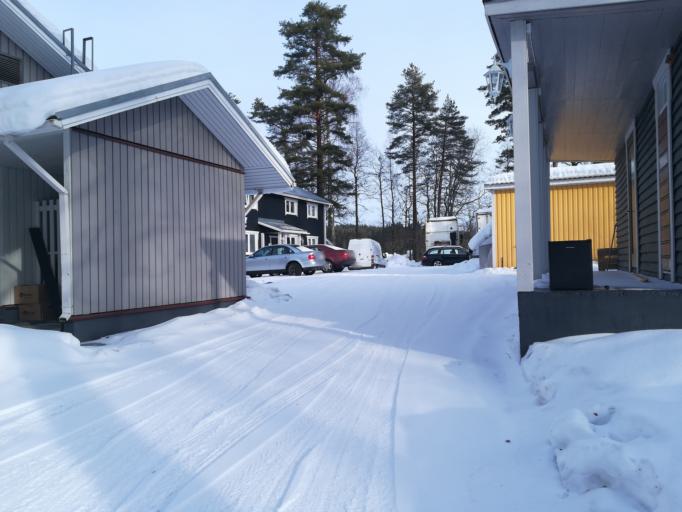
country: FI
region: Southern Savonia
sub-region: Savonlinna
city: Savonlinna
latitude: 61.8290
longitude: 29.0242
